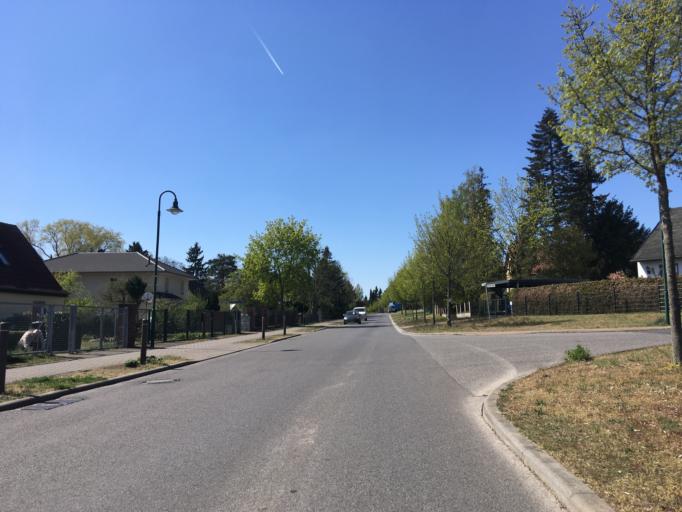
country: DE
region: Berlin
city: Buch
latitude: 52.6577
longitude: 13.5282
